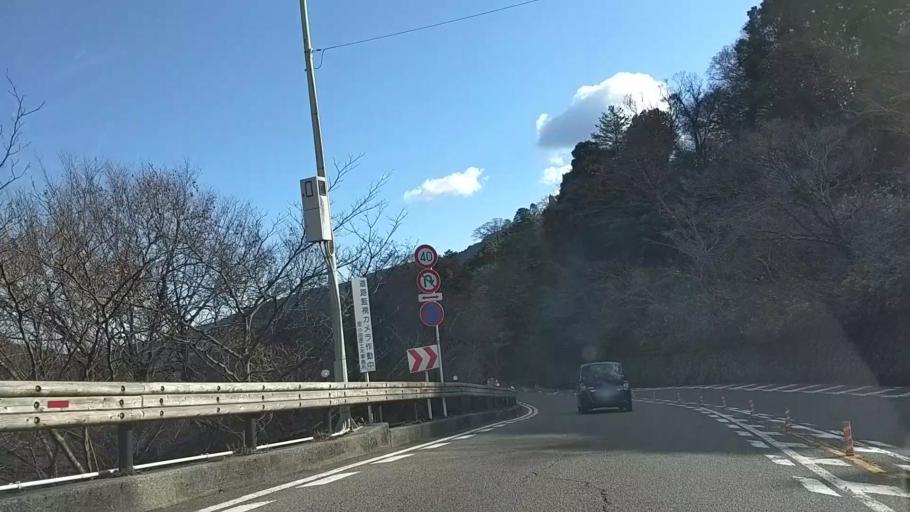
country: JP
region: Kanagawa
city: Hakone
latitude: 35.2404
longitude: 139.0727
